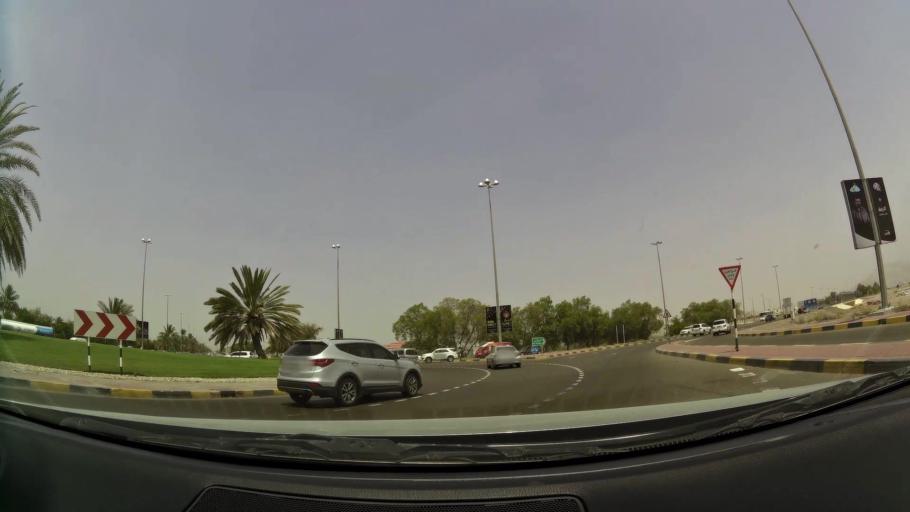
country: AE
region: Abu Dhabi
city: Al Ain
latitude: 24.1910
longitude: 55.6962
